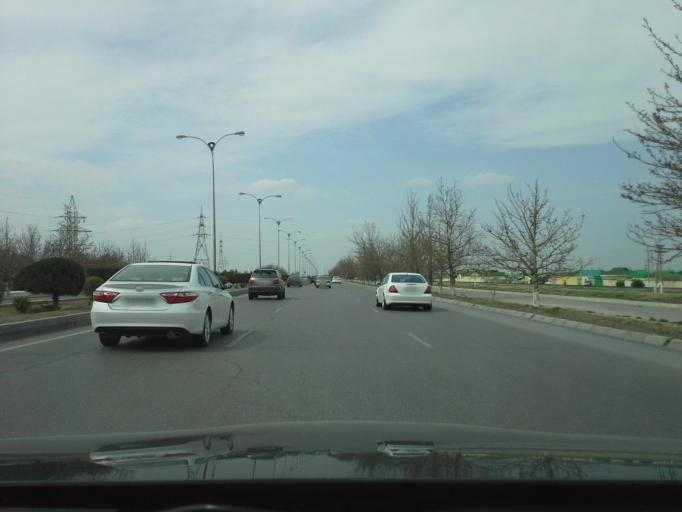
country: TM
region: Ahal
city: Abadan
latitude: 38.0620
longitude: 58.1695
